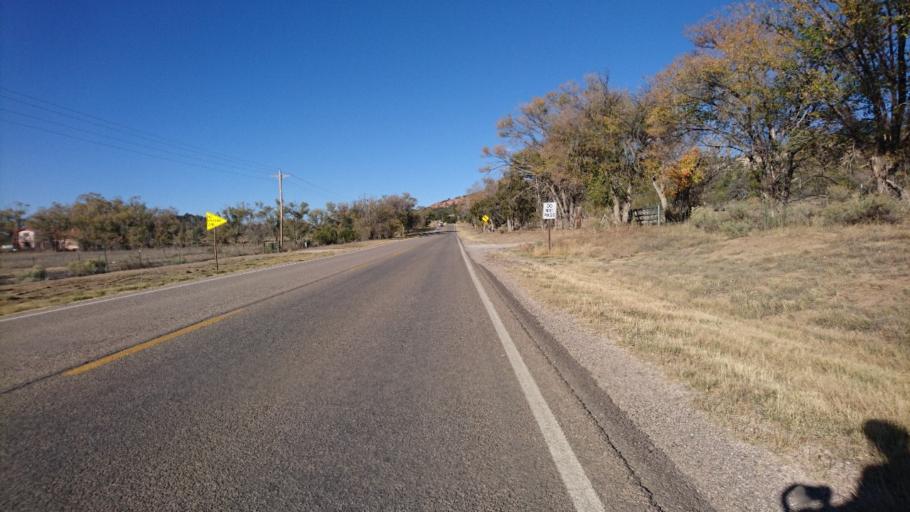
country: US
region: New Mexico
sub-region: McKinley County
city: Black Rock
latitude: 35.1333
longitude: -108.5116
